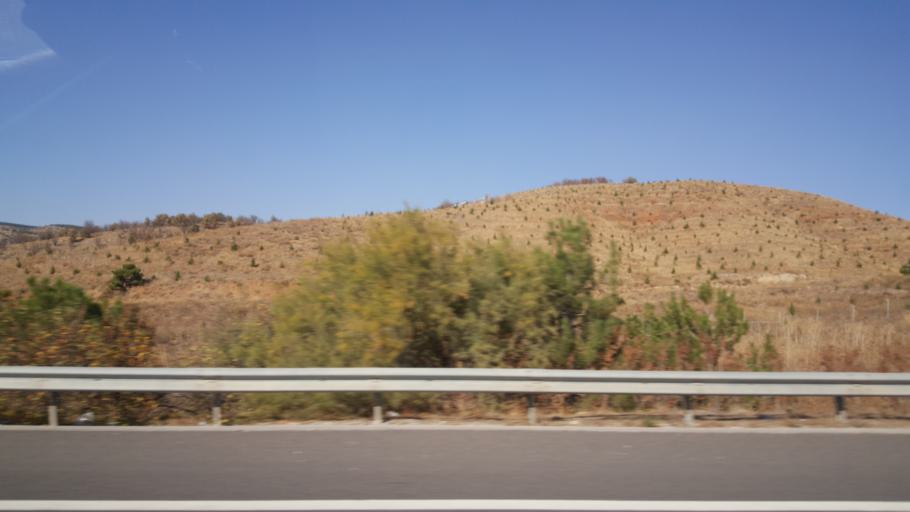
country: TR
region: Ankara
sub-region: Goelbasi
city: Golbasi
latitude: 39.8125
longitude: 32.8238
